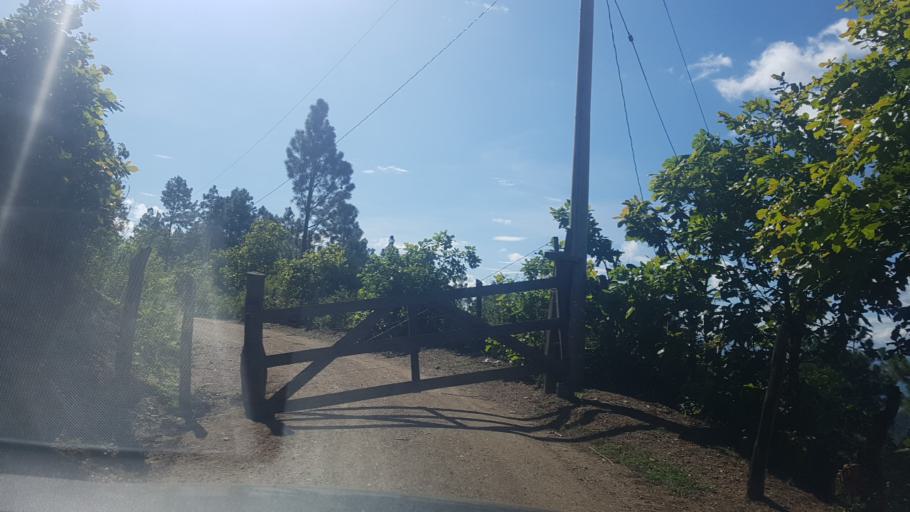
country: NI
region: Nueva Segovia
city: Ocotal
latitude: 13.6429
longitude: -86.6410
